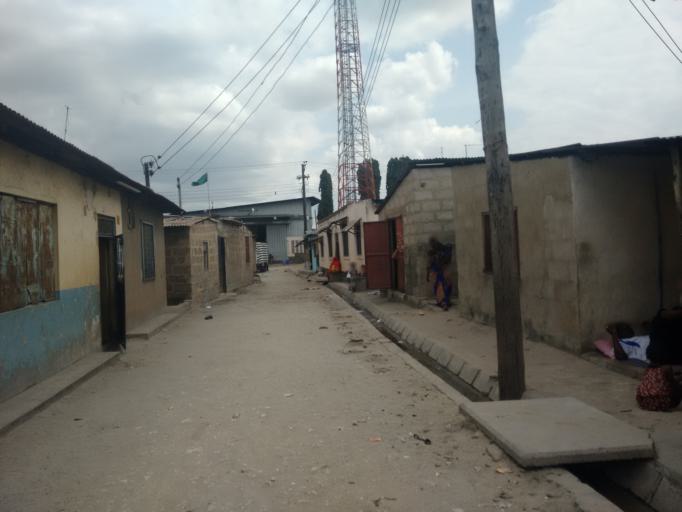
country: TZ
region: Dar es Salaam
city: Dar es Salaam
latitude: -6.8544
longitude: 39.2511
